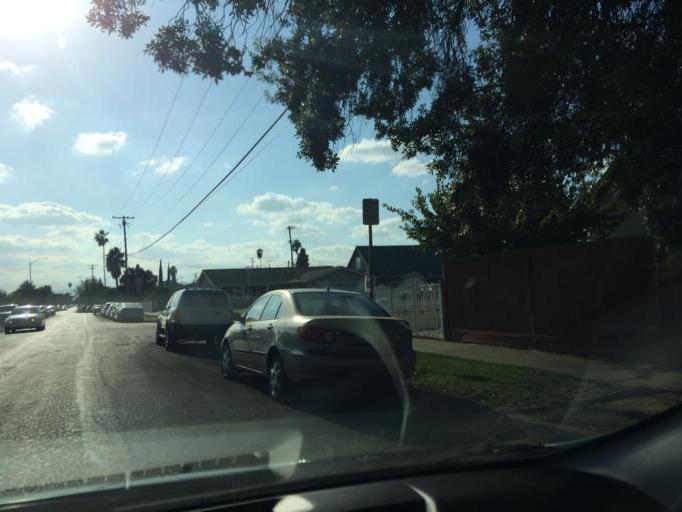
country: US
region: California
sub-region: Santa Clara County
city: Alum Rock
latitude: 37.3303
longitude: -121.8225
